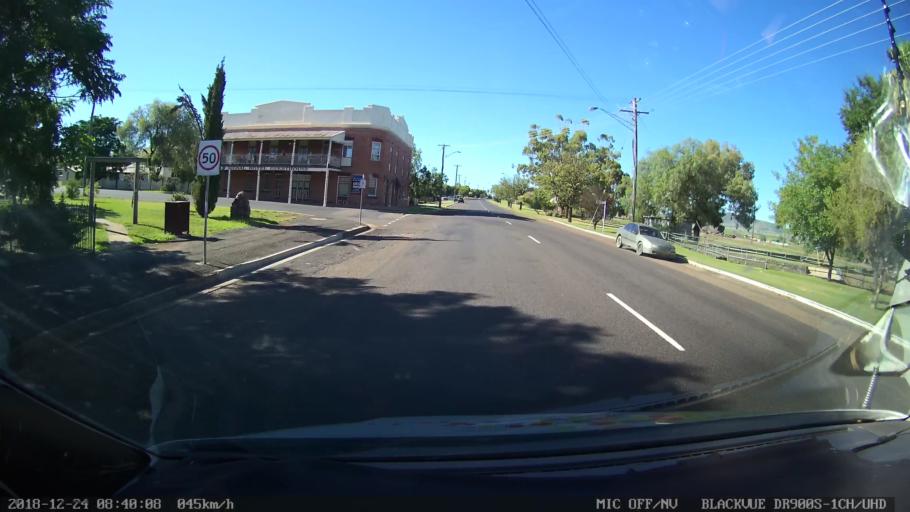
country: AU
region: New South Wales
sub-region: Liverpool Plains
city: Quirindi
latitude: -31.3527
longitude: 150.6469
